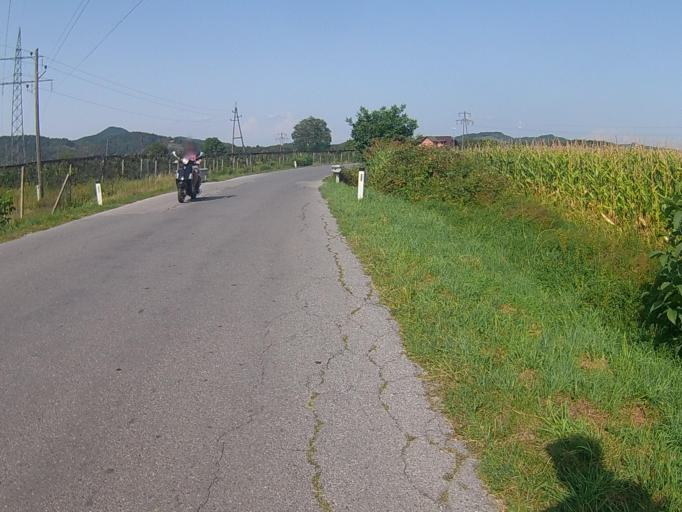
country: SI
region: Maribor
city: Pekre
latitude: 46.5556
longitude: 15.6006
